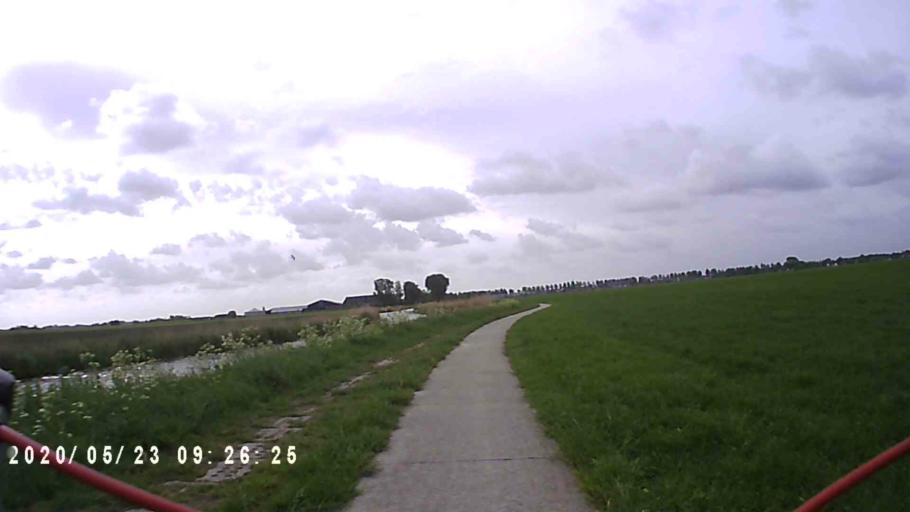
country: NL
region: Groningen
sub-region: Gemeente Bedum
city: Bedum
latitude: 53.2934
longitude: 6.6949
